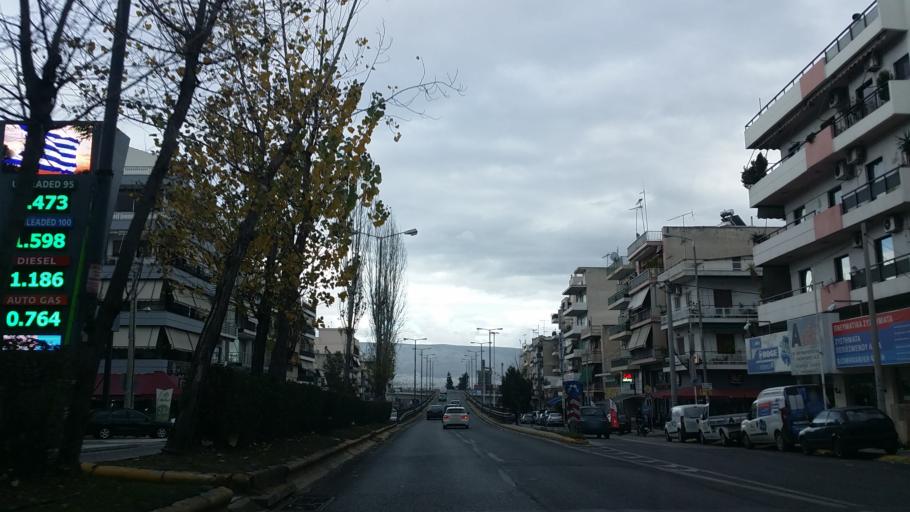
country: GR
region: Attica
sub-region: Nomos Piraios
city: Agios Ioannis Rentis
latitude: 37.9773
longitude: 23.6641
